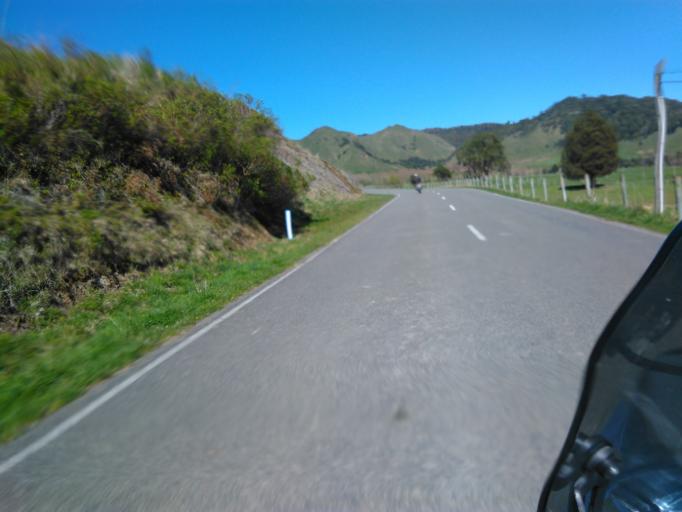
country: NZ
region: Bay of Plenty
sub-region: Opotiki District
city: Opotiki
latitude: -38.2997
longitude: 177.5218
